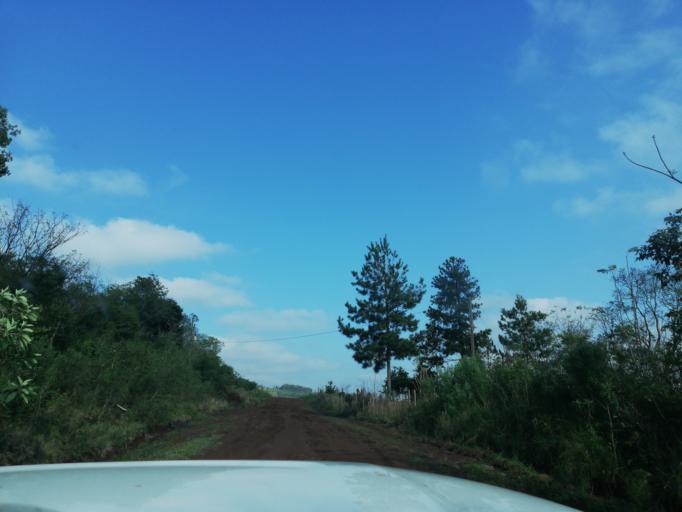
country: AR
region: Misiones
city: Cerro Azul
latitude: -27.5993
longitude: -55.5276
